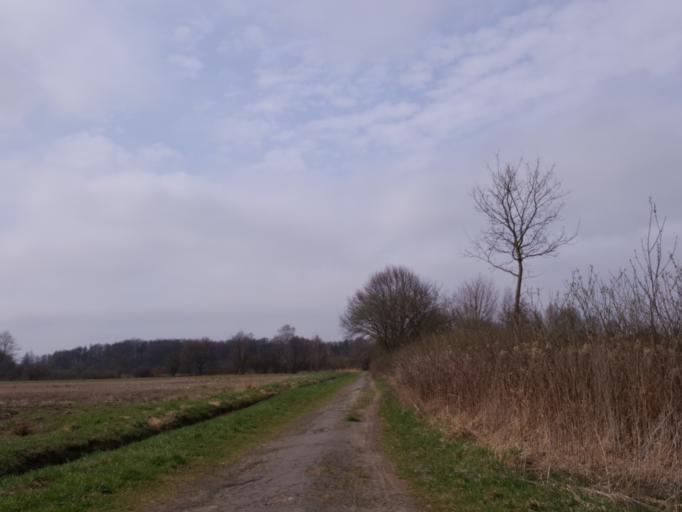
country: DE
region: Schleswig-Holstein
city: Oststeinbek
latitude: 53.5060
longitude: 10.1412
